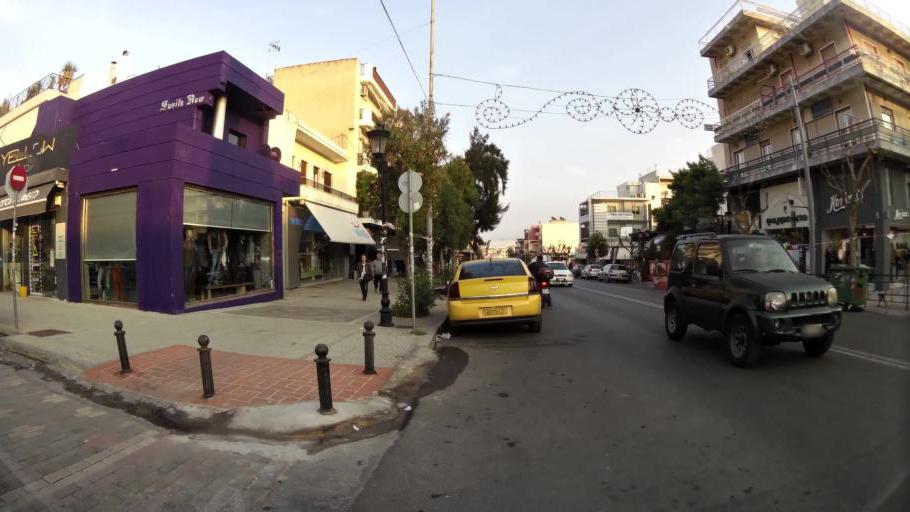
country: GR
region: Attica
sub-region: Nomarchia Athinas
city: Petroupolis
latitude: 38.0403
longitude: 23.6884
